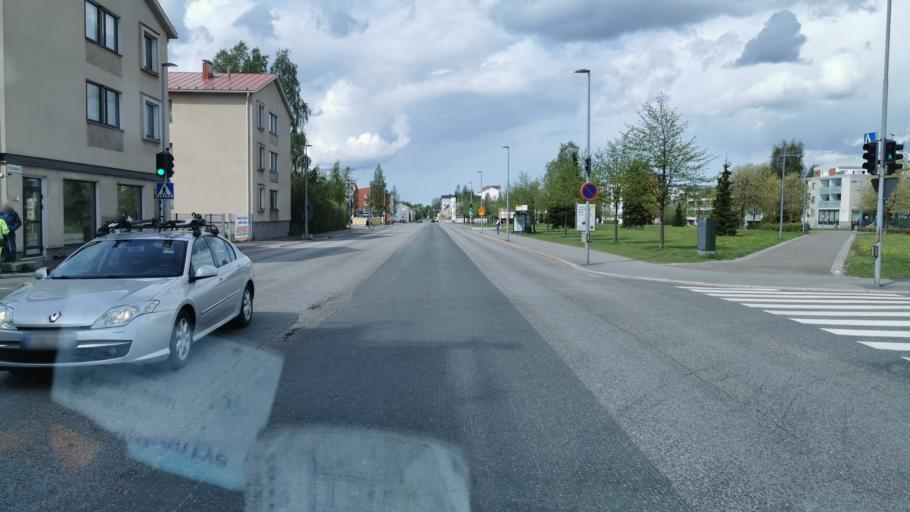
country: FI
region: Northern Ostrobothnia
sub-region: Oulu
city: Oulu
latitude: 65.0043
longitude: 25.4621
